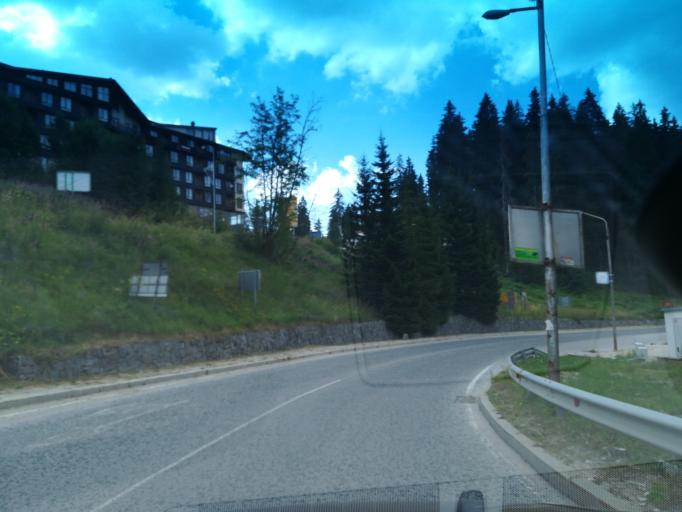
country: BG
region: Smolyan
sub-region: Obshtina Smolyan
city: Smolyan
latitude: 41.6507
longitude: 24.6953
